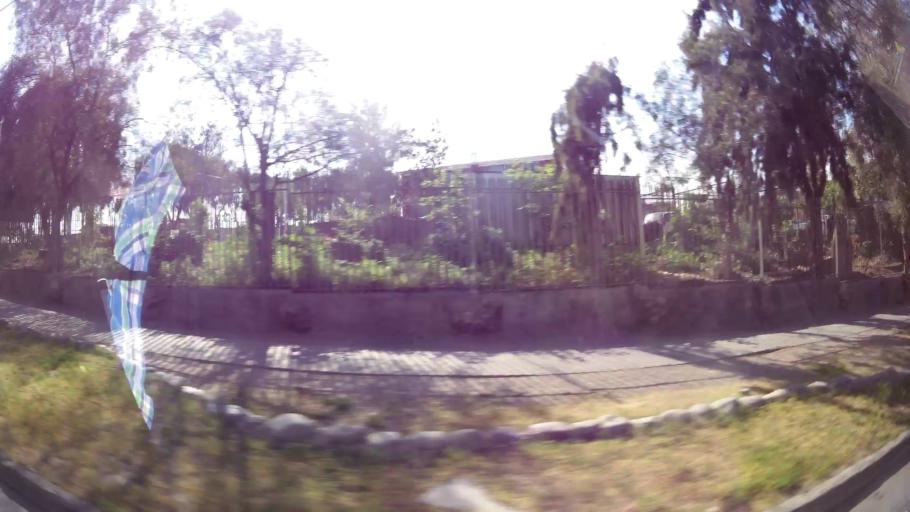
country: CL
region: Santiago Metropolitan
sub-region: Provincia de Santiago
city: Lo Prado
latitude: -33.4444
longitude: -70.7635
